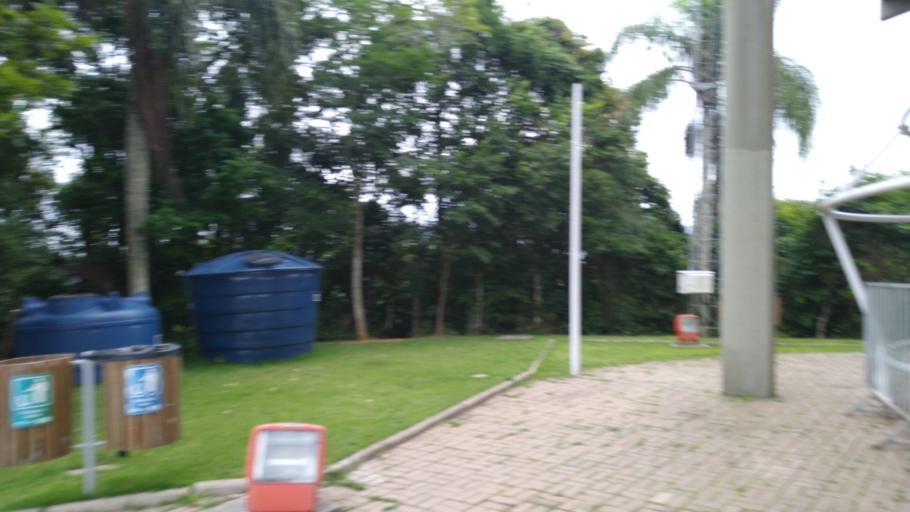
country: BR
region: Santa Catarina
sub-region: Itapema
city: Itapema
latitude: -27.0877
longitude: -48.6036
